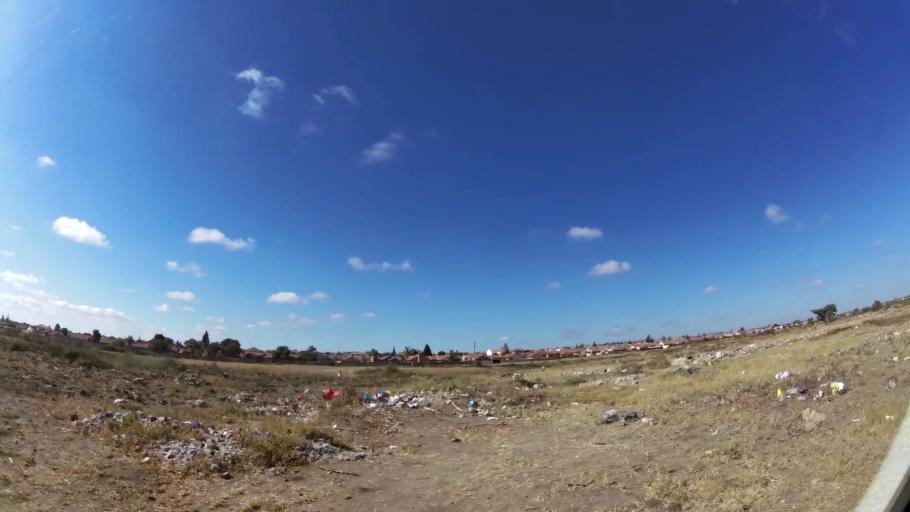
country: ZA
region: Limpopo
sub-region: Capricorn District Municipality
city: Polokwane
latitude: -23.8620
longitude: 29.3972
